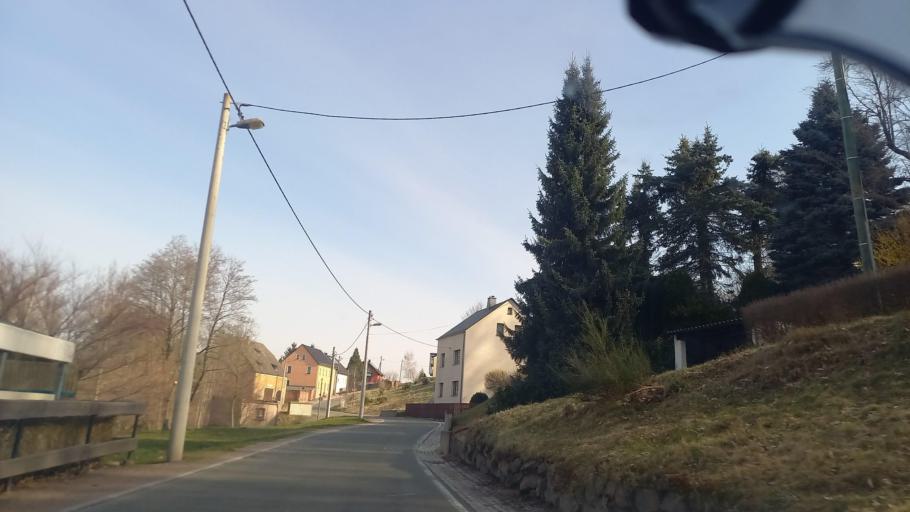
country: DE
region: Saxony
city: Kirchberg
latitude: 50.6160
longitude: 12.5217
